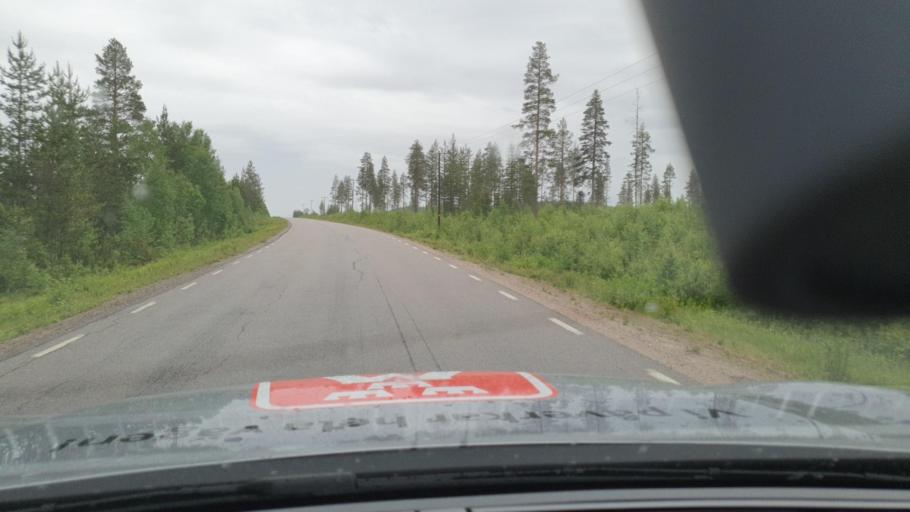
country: SE
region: Norrbotten
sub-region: Pajala Kommun
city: Pajala
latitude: 66.7608
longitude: 23.1547
